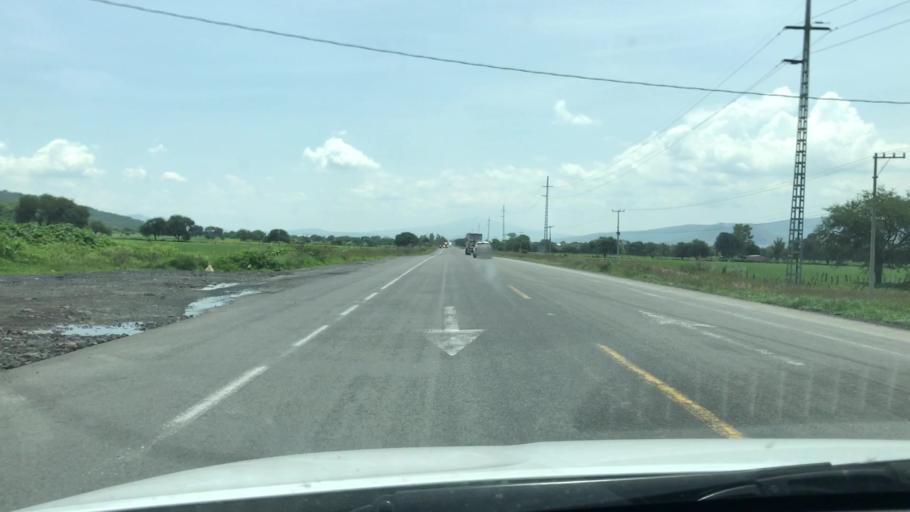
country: MX
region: Michoacan
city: Vistahermosa de Negrete
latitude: 20.2710
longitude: -102.4291
